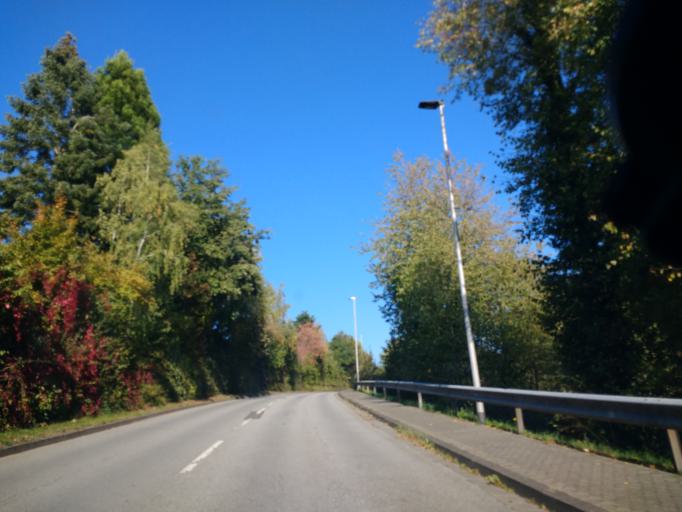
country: DE
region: Rheinland-Pfalz
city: Konz
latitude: 49.6987
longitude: 6.5930
